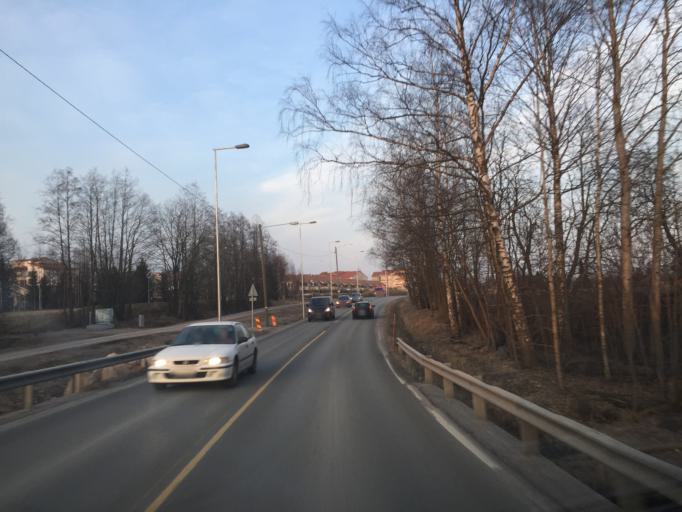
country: FI
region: Uusimaa
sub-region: Helsinki
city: Vantaa
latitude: 60.2849
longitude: 24.9424
